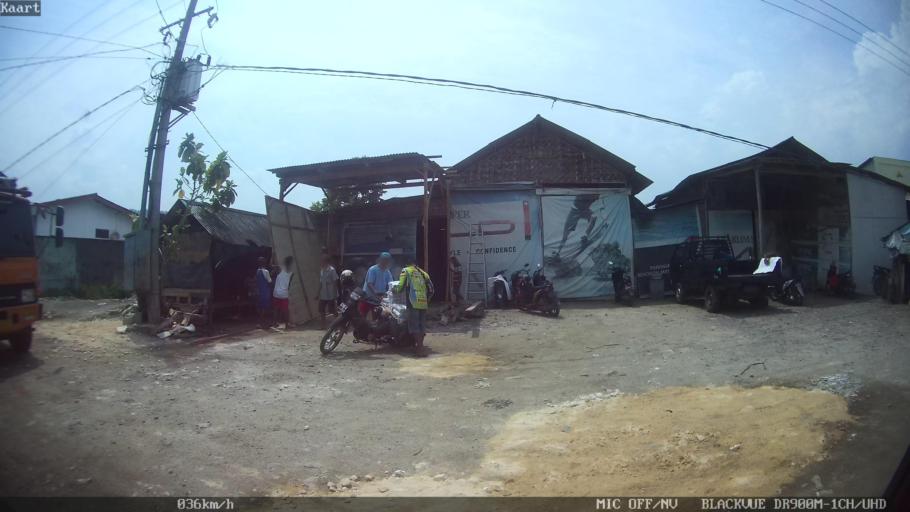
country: ID
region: Lampung
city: Bandarlampung
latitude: -5.4521
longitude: 105.2493
